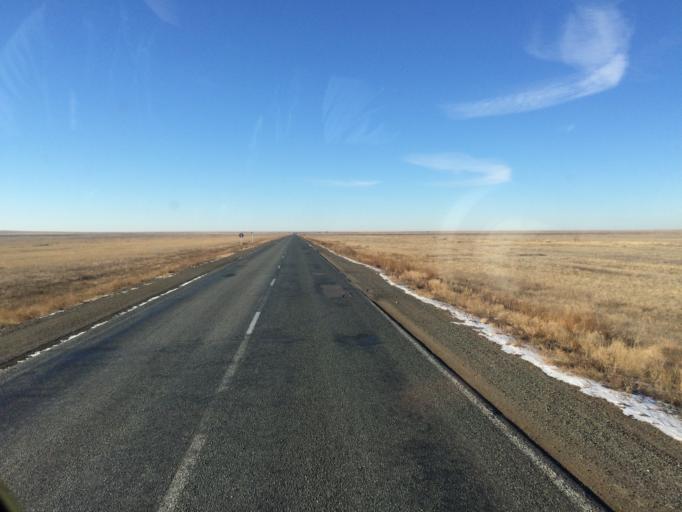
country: KZ
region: Aqtoebe
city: Khromtau
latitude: 50.1837
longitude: 58.6607
